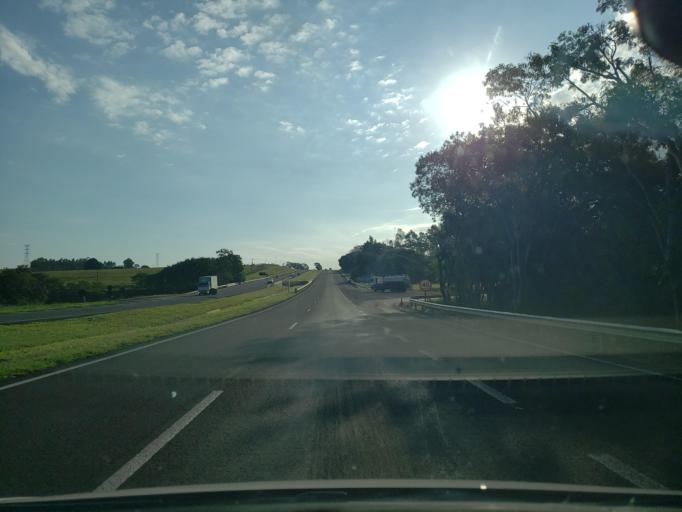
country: BR
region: Sao Paulo
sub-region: Valparaiso
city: Valparaiso
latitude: -21.2097
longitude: -50.8734
